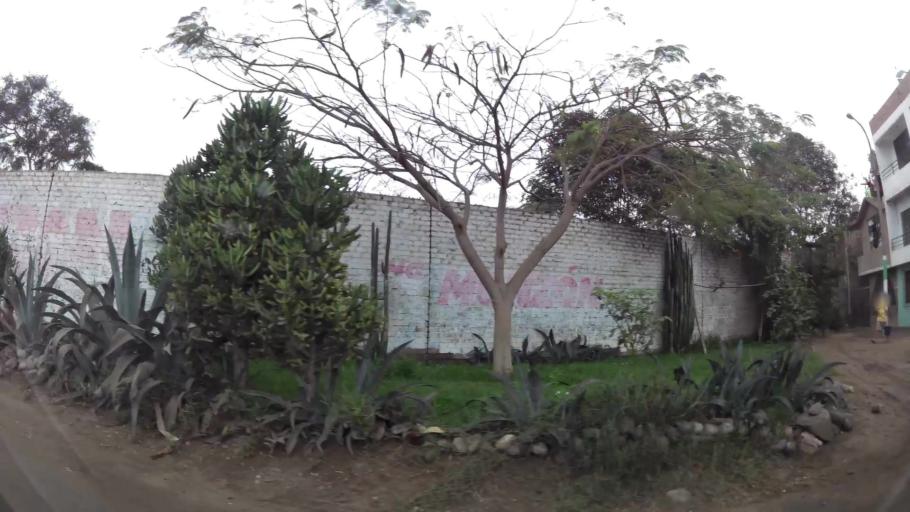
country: PE
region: Lima
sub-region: Lima
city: Carabayllo
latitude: -11.8721
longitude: -77.0743
